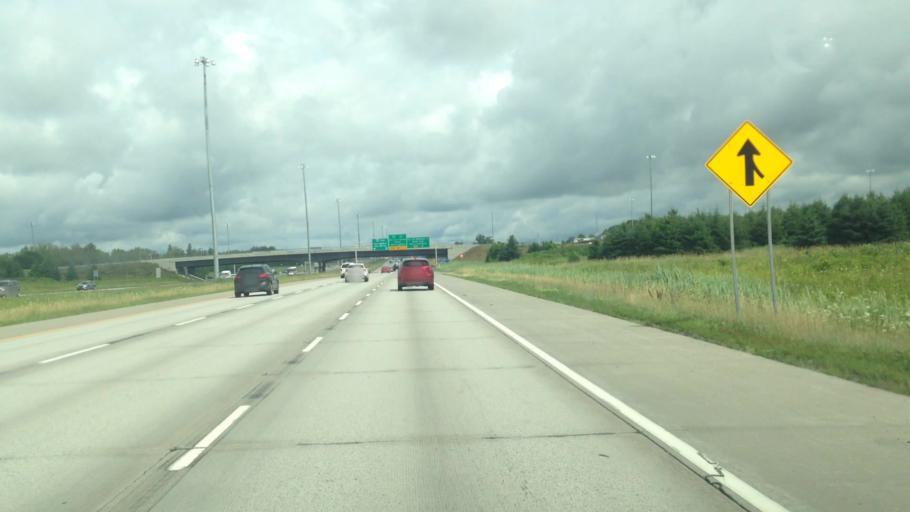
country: CA
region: Quebec
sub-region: Laurentides
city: Saint-Jerome
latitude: 45.7761
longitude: -74.0202
